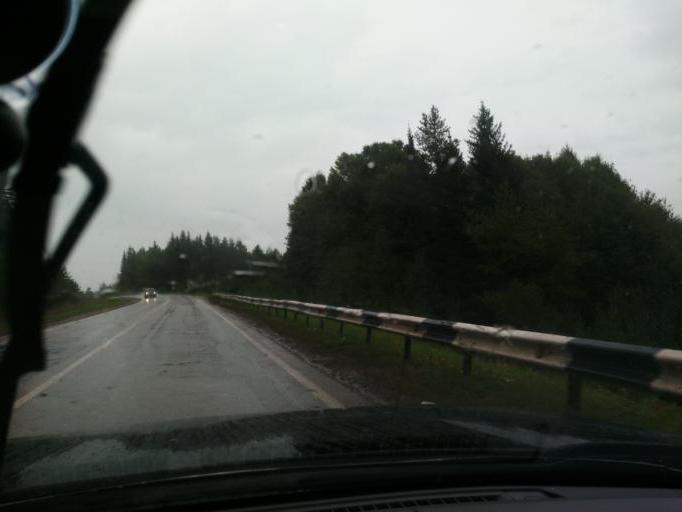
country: RU
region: Perm
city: Osa
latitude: 57.3046
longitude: 55.6182
